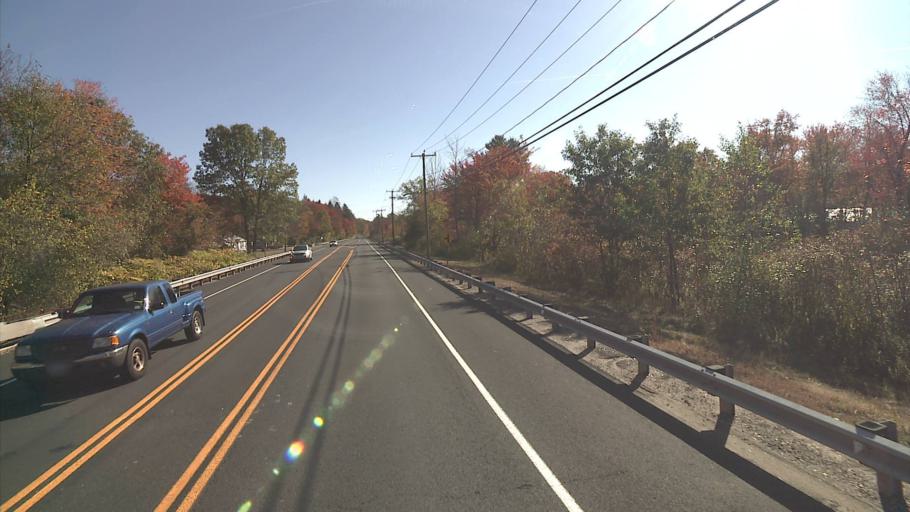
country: US
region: Connecticut
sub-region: Tolland County
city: Rockville
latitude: 41.7840
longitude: -72.4339
